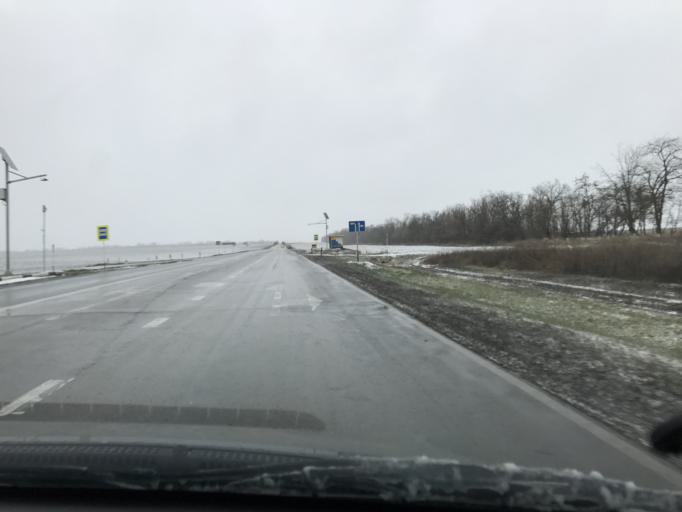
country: RU
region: Rostov
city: Yegorlykskaya
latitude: 46.6587
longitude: 40.5568
